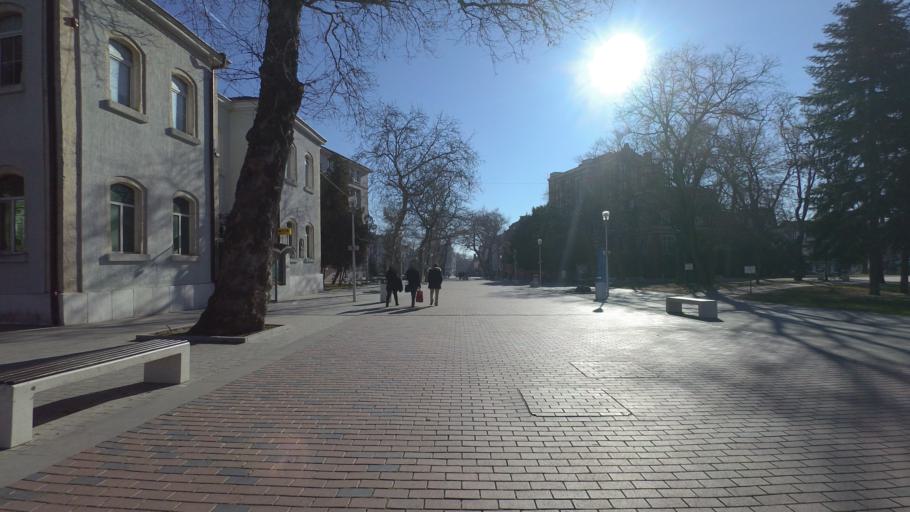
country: BG
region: Varna
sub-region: Obshtina Varna
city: Varna
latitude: 43.2044
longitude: 27.9111
